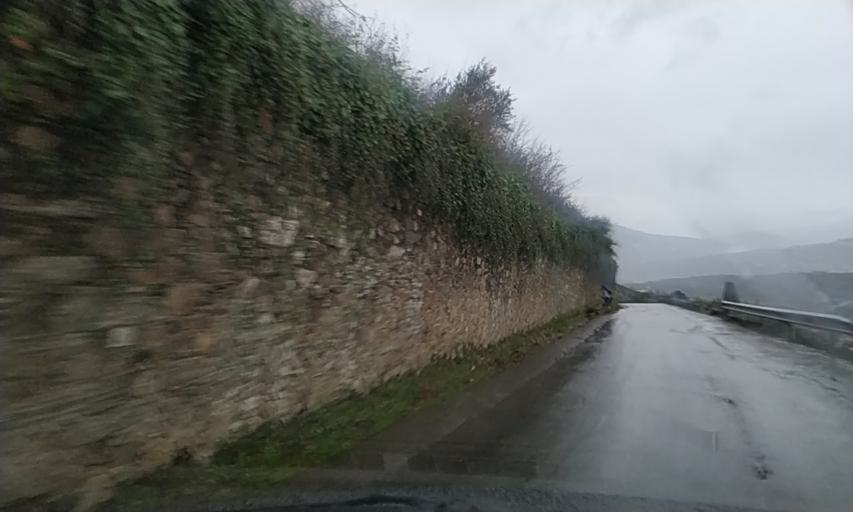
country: PT
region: Vila Real
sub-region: Peso da Regua
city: Peso da Regua
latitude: 41.1687
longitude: -7.7448
